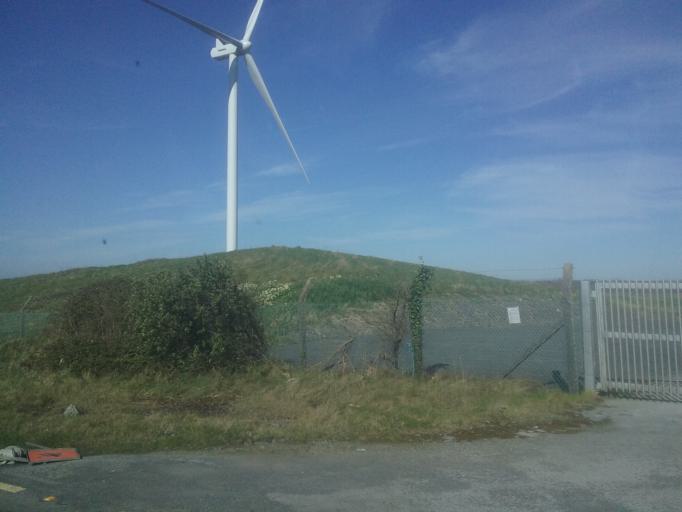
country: IE
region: Munster
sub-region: An Clar
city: Kilrush
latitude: 52.6121
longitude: -9.4312
